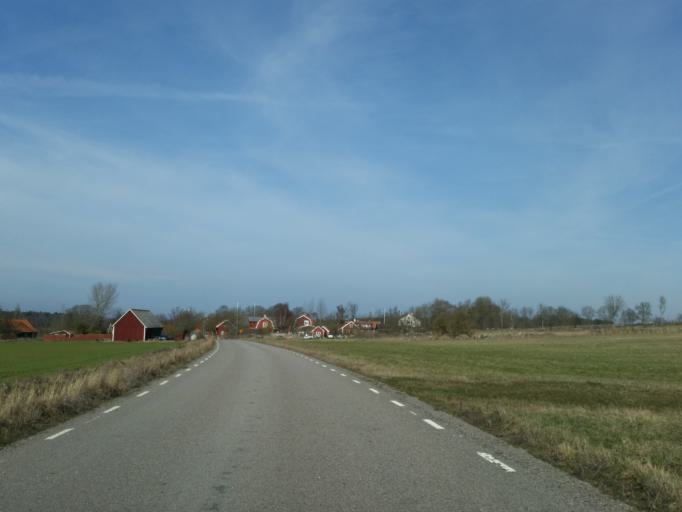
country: SE
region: Kalmar
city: Faerjestaden
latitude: 56.7343
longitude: 16.5421
